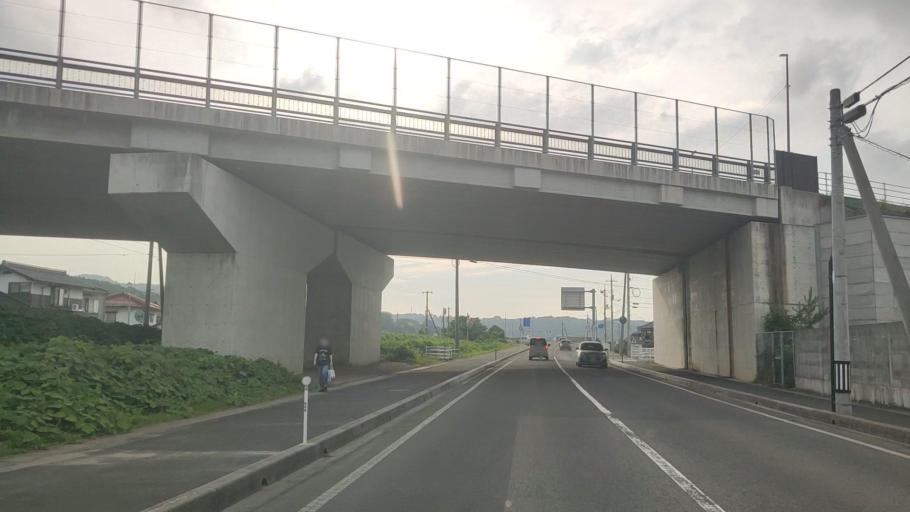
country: JP
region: Tottori
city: Kurayoshi
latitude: 35.4566
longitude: 133.8452
